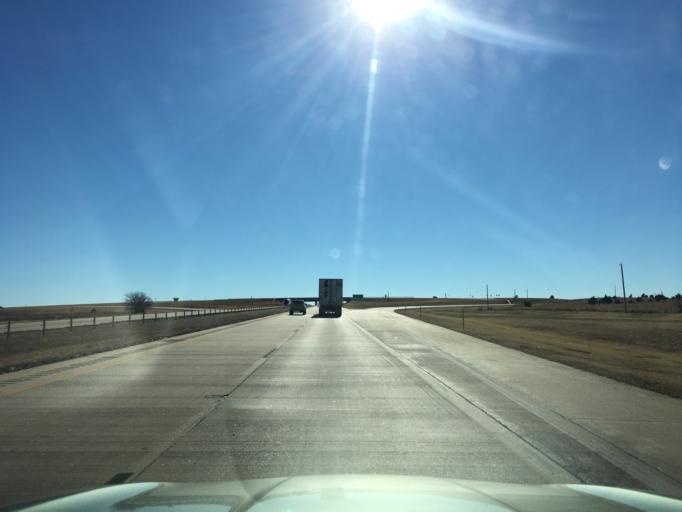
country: US
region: Oklahoma
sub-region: Noble County
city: Perry
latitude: 36.4055
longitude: -97.3272
